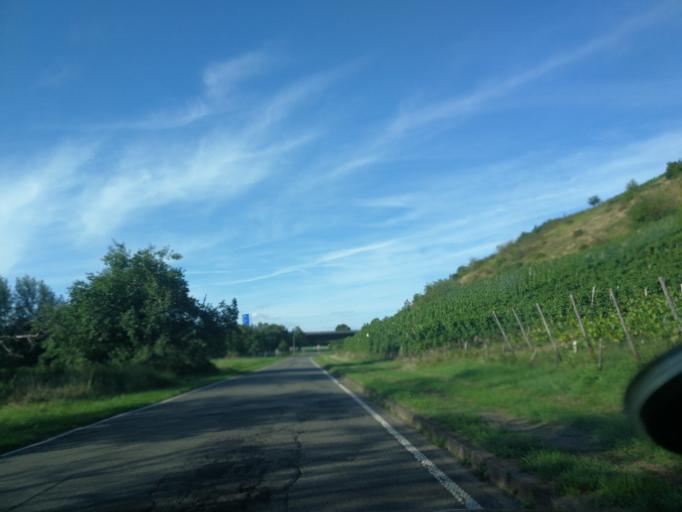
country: DE
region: Rheinland-Pfalz
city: Schweich
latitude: 49.8090
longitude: 6.7438
